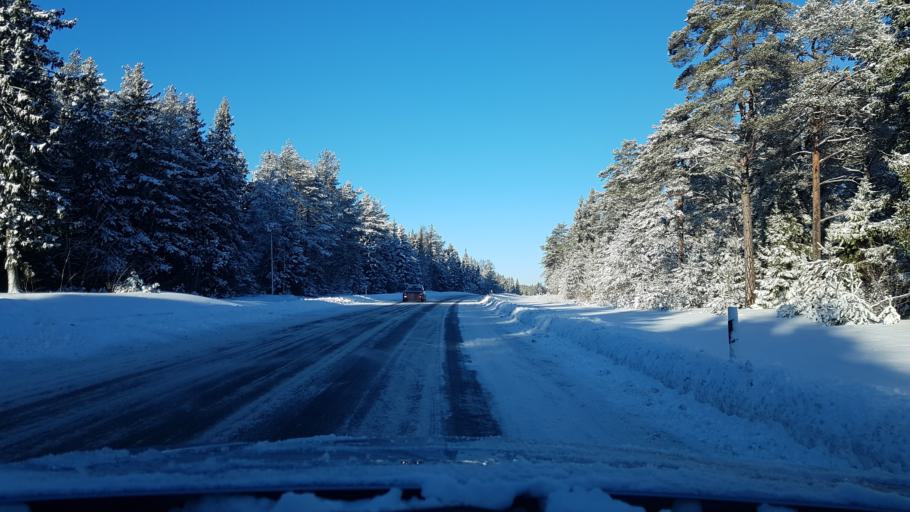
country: EE
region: Hiiumaa
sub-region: Kaerdla linn
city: Kardla
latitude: 58.9653
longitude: 22.8359
